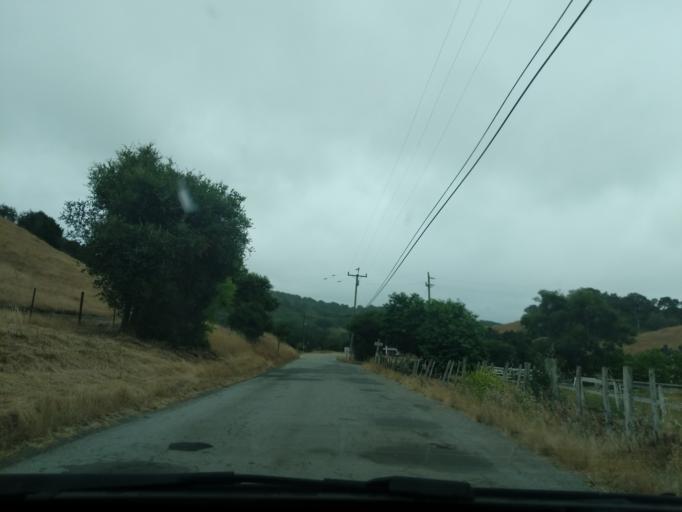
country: US
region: California
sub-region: San Benito County
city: Aromas
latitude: 36.8642
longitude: -121.6222
